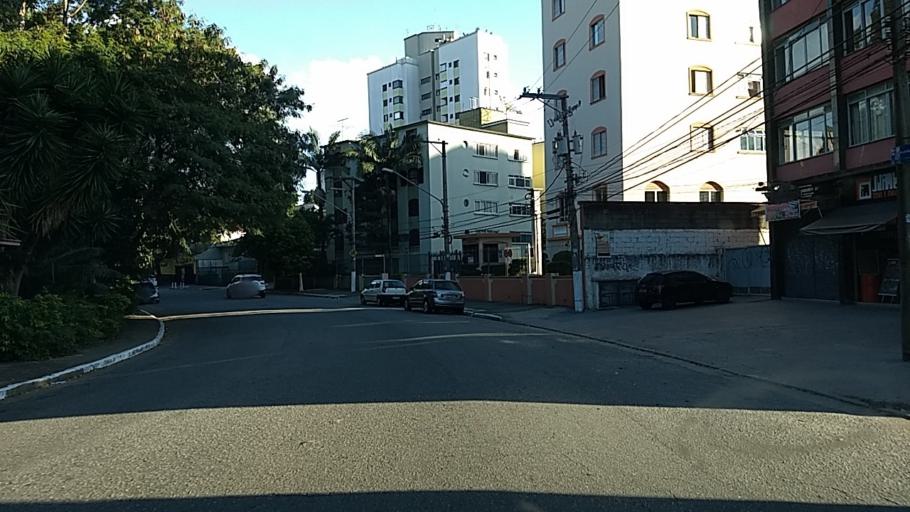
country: BR
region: Sao Paulo
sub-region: Sao Paulo
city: Sao Paulo
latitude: -23.4907
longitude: -46.6120
